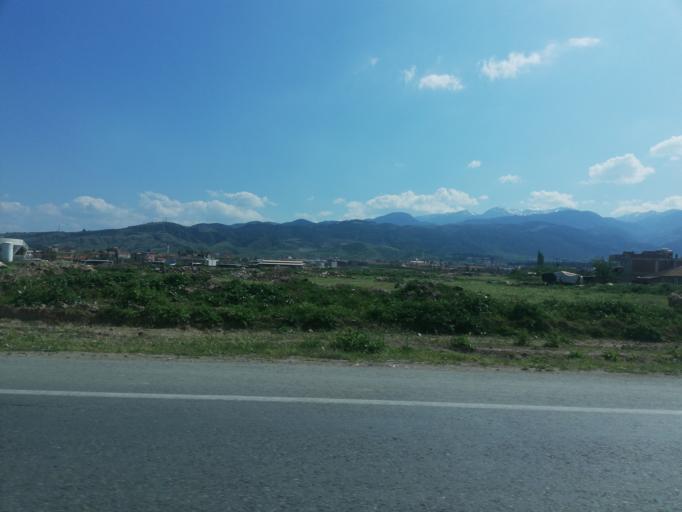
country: TR
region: Manisa
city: Alasehir
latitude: 38.3593
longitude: 28.5367
